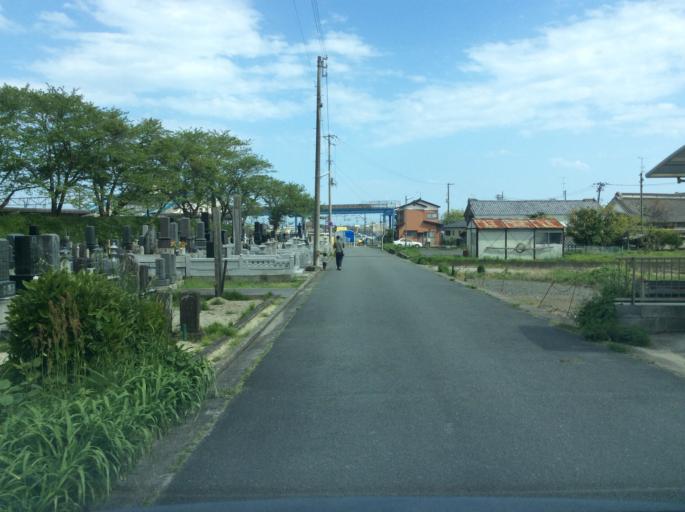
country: JP
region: Ibaraki
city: Kitaibaraki
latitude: 36.8842
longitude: 140.7857
